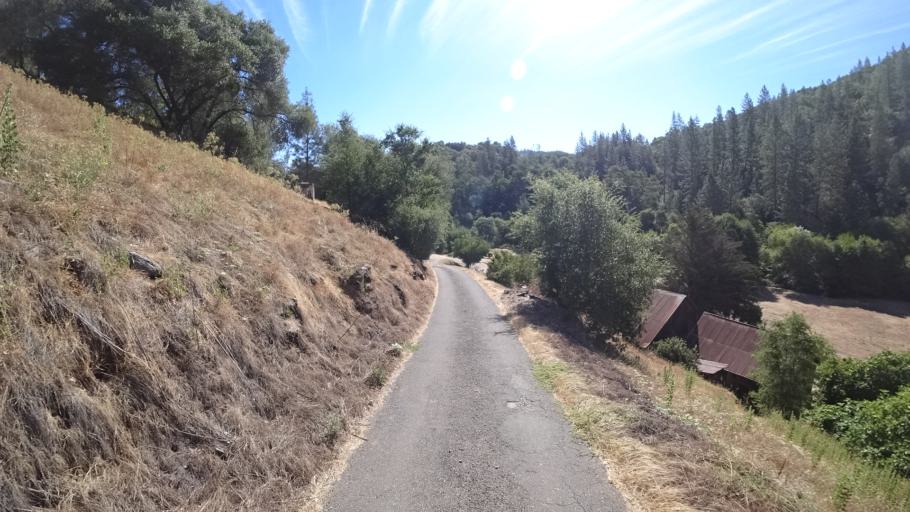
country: US
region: California
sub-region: Calaveras County
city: Mountain Ranch
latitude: 38.1631
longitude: -120.5383
